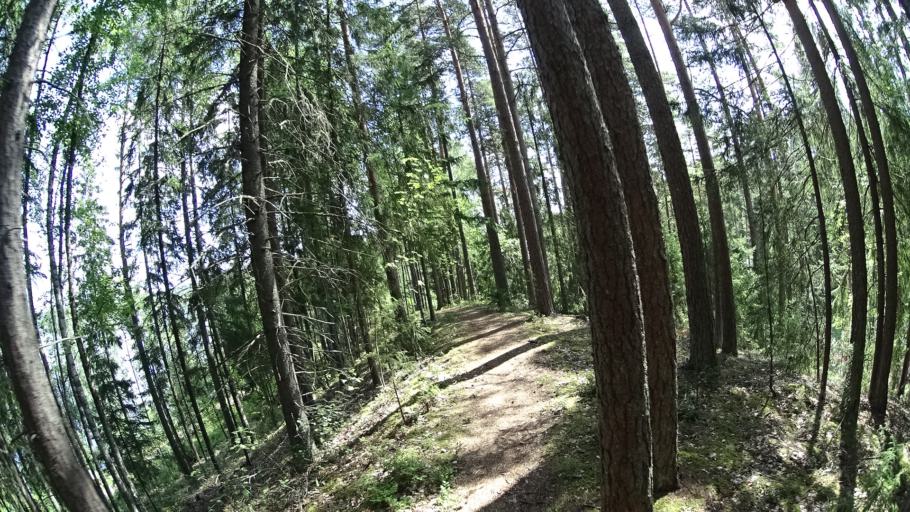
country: FI
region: Haeme
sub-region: Forssa
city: Tammela
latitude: 60.7677
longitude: 23.8824
